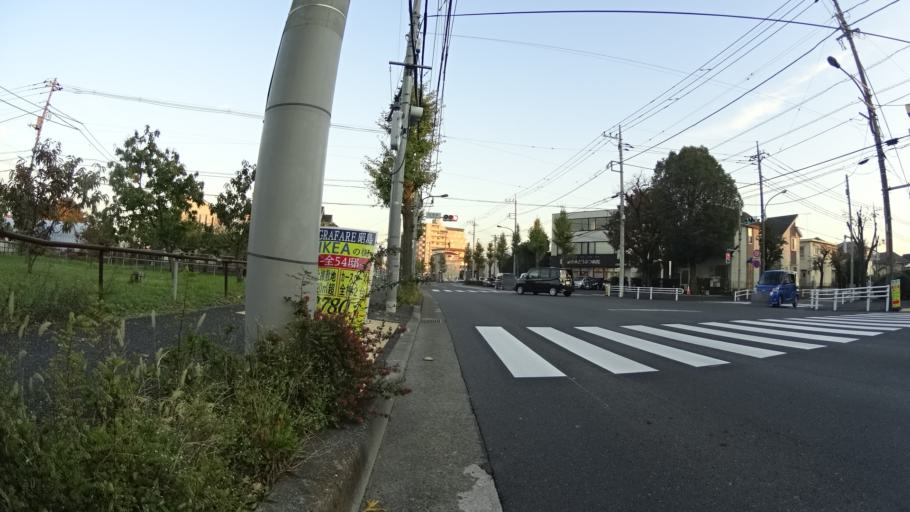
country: JP
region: Tokyo
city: Fussa
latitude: 35.7023
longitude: 139.3575
